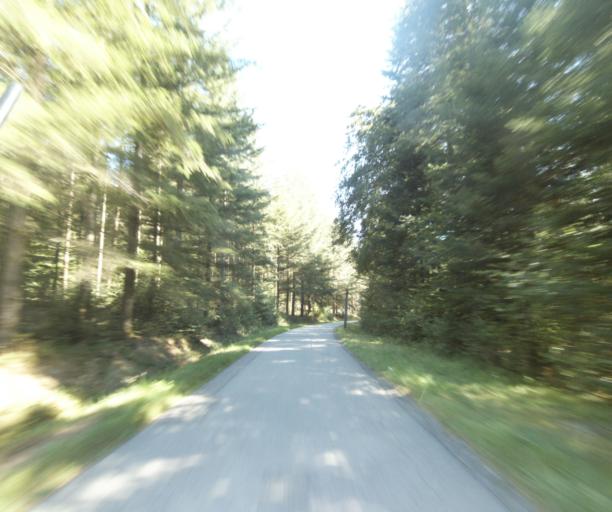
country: FR
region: Lorraine
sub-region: Departement des Vosges
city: Deyvillers
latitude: 48.1634
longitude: 6.5271
